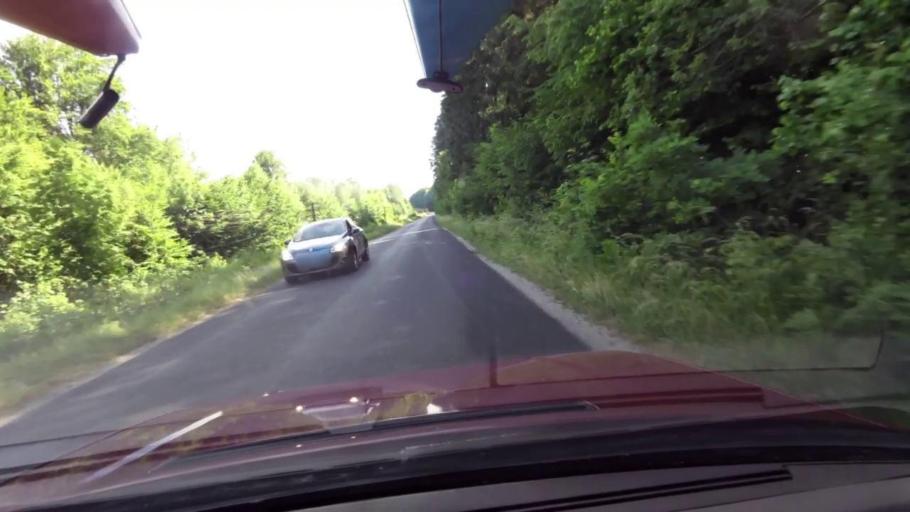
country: PL
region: Pomeranian Voivodeship
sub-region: Powiat slupski
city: Kepice
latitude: 54.1997
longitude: 16.8882
